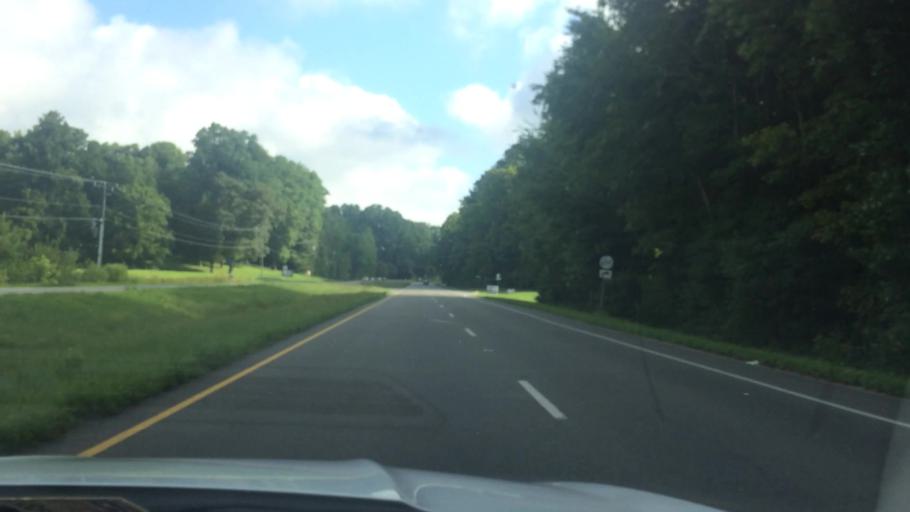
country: US
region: Virginia
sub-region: Gloucester County
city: Gloucester Courthouse
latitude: 37.4483
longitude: -76.4726
